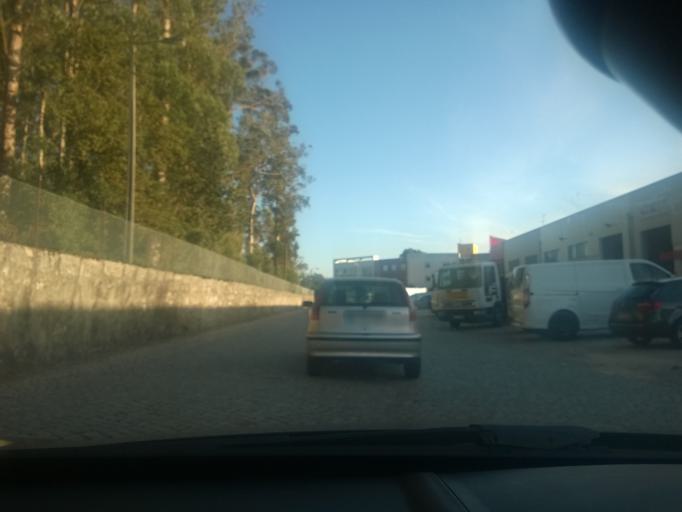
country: PT
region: Porto
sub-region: Maia
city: Anta
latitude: 41.2748
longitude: -8.6099
